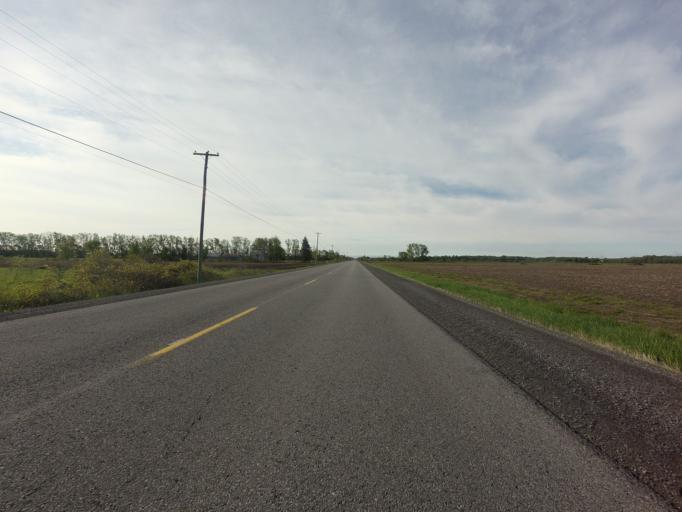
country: CA
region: Ontario
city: Ottawa
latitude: 45.3037
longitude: -75.4556
